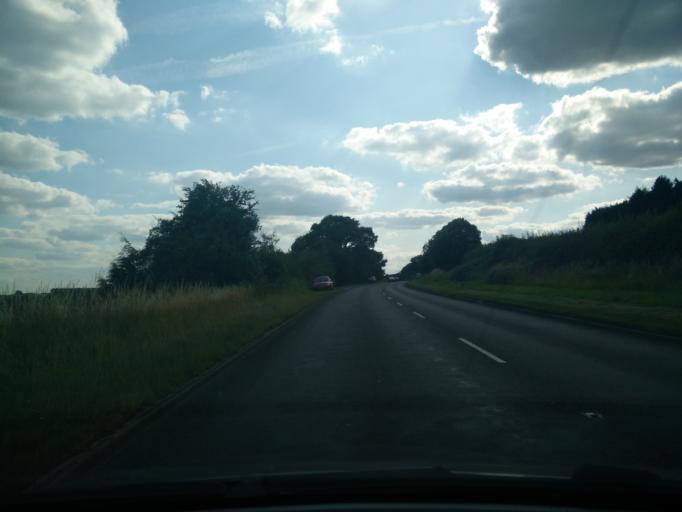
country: GB
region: England
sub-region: Derbyshire
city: West Hallam
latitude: 52.9536
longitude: -1.3469
